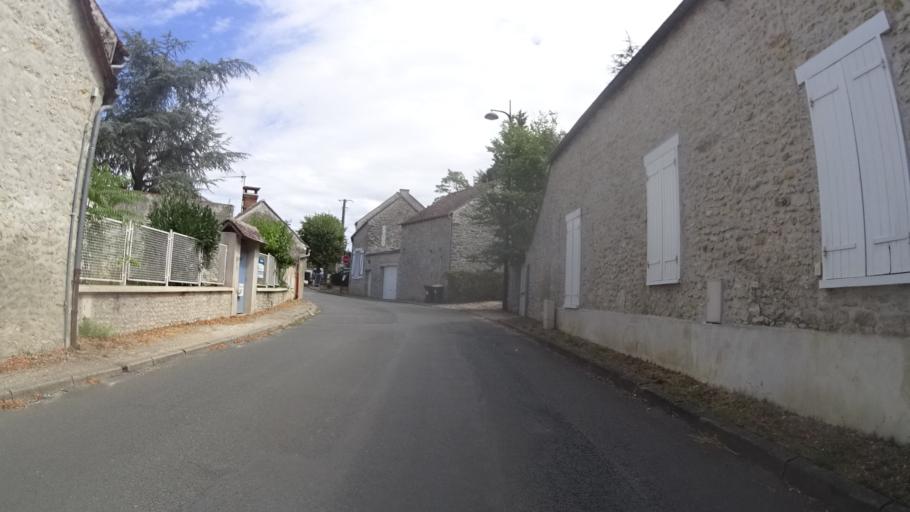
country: FR
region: Centre
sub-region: Departement du Loiret
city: Malesherbes
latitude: 48.2862
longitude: 2.4298
